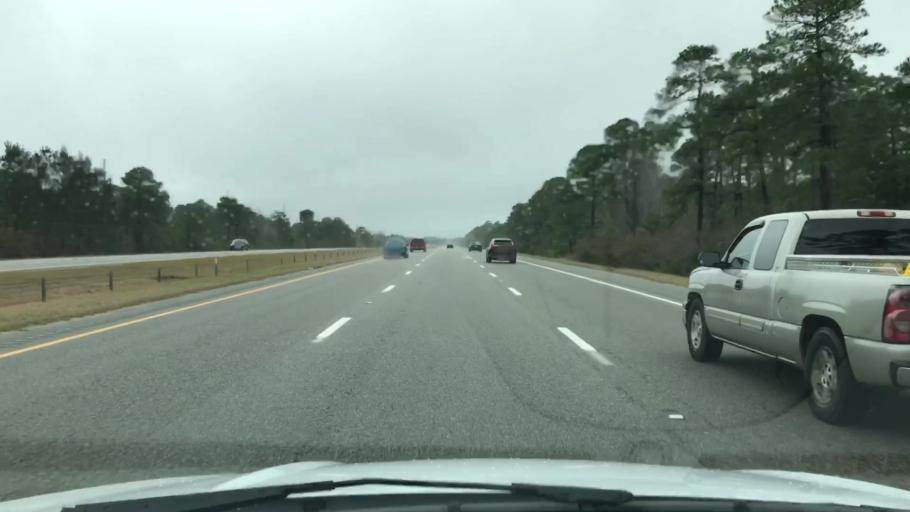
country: US
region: South Carolina
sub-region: Horry County
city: Forestbrook
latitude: 33.7481
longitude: -78.9089
